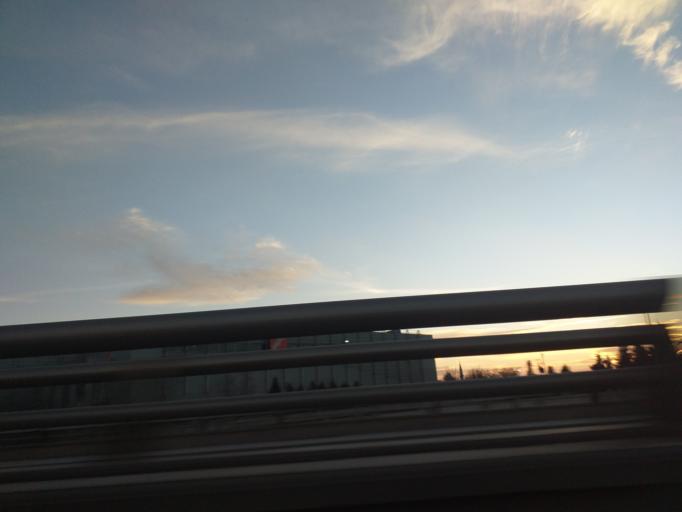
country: TR
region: Ankara
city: Ankara
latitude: 39.9539
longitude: 32.8315
